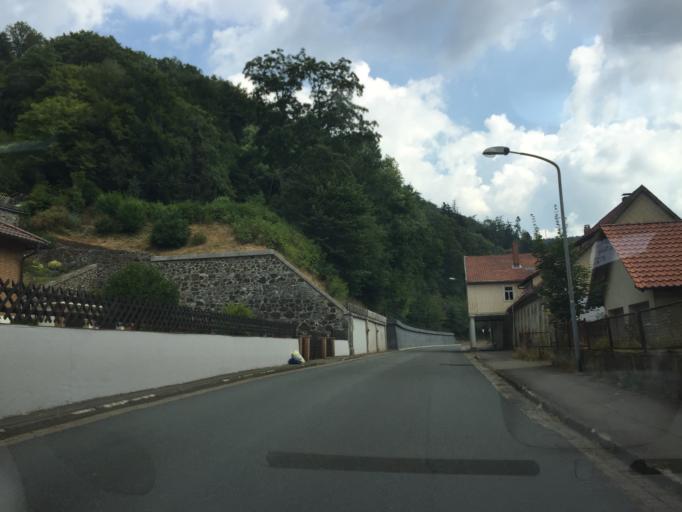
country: DE
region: Lower Saxony
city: Zorge
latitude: 51.6383
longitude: 10.6344
